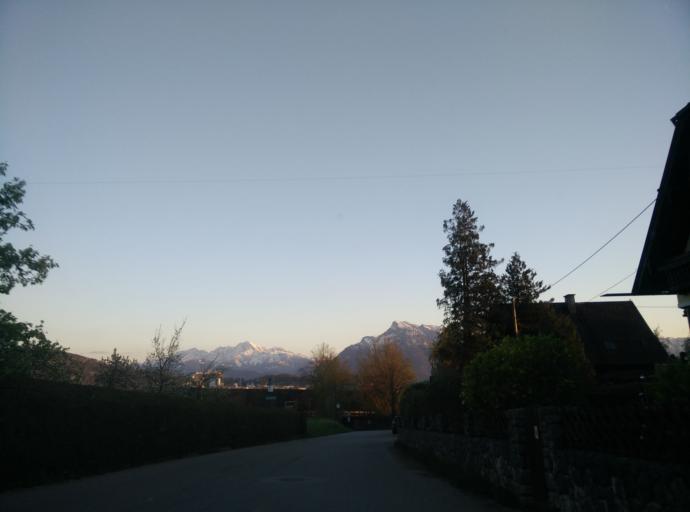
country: AT
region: Salzburg
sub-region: Politischer Bezirk Salzburg-Umgebung
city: Bergheim
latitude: 47.8315
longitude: 13.0400
